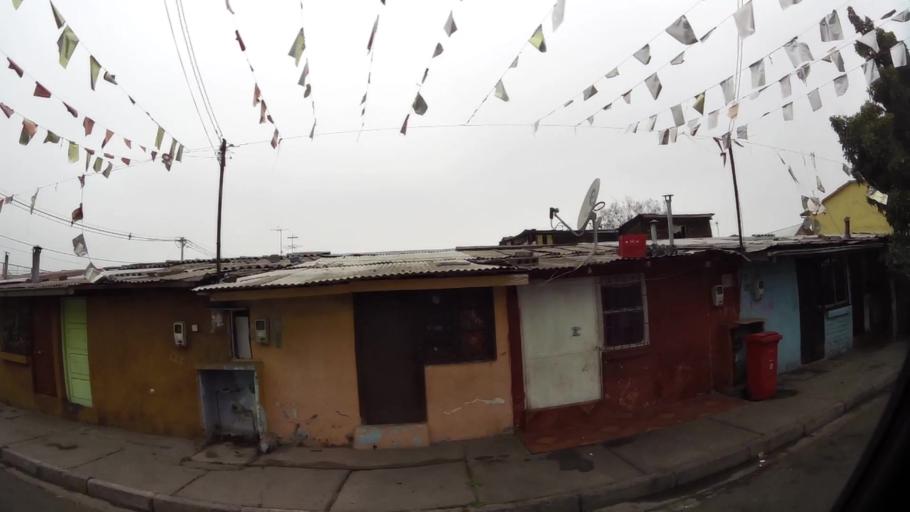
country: CL
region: Santiago Metropolitan
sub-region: Provincia de Santiago
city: Santiago
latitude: -33.4847
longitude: -70.6380
